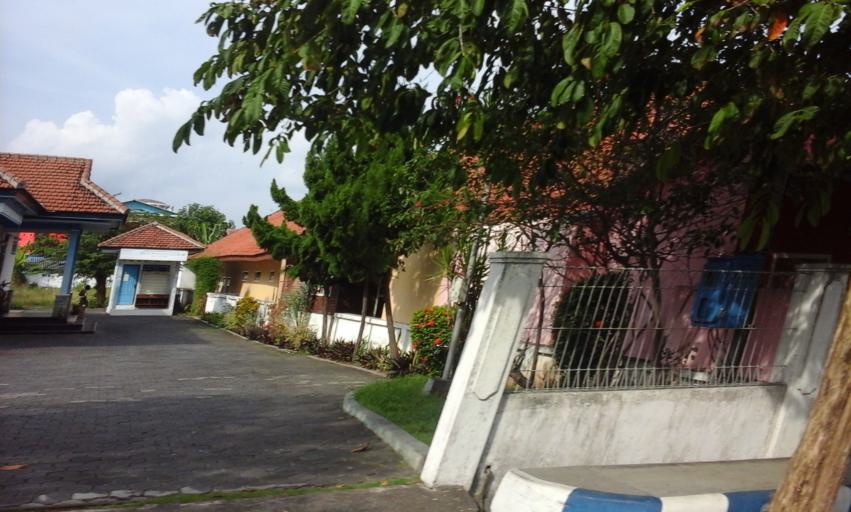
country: ID
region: East Java
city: Krajan Satu
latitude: -8.2101
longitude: 114.3503
